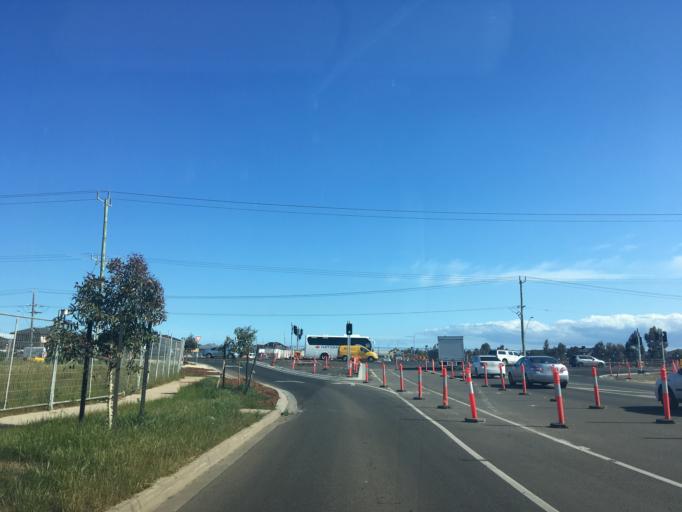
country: AU
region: Victoria
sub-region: Wyndham
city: Truganina
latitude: -37.8380
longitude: 144.7401
